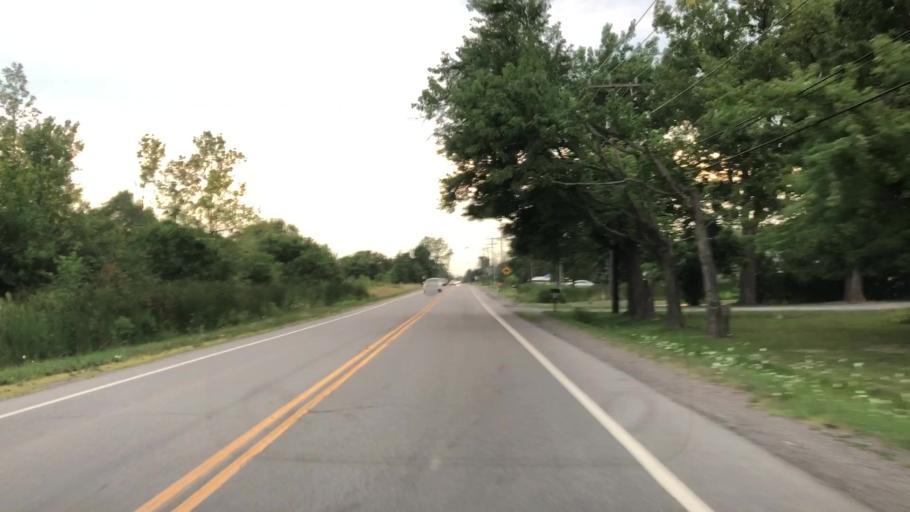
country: US
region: New York
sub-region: Erie County
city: Elma Center
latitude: 42.8390
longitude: -78.6762
